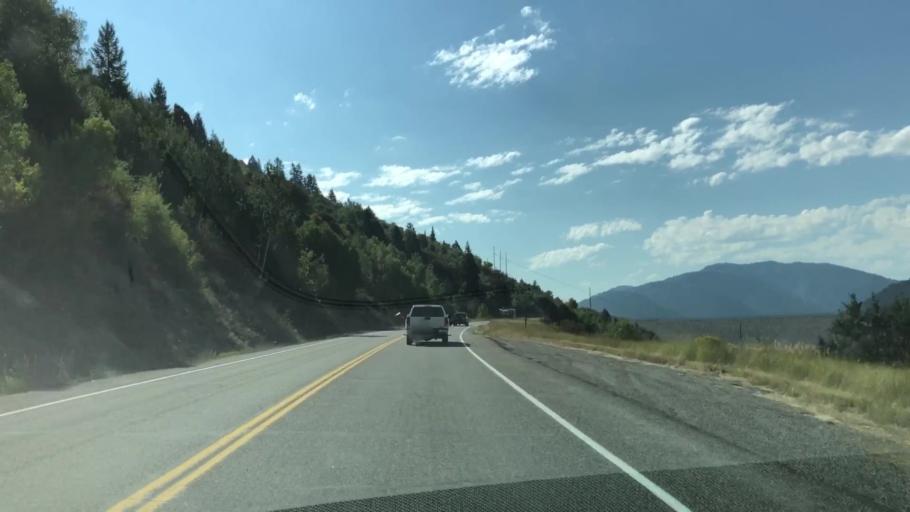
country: US
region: Idaho
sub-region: Teton County
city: Victor
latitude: 43.3404
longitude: -111.2011
